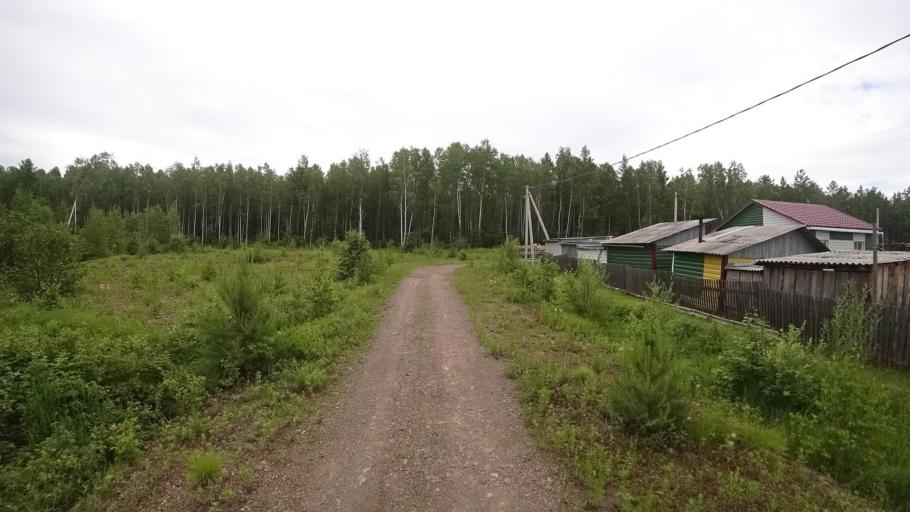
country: RU
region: Khabarovsk Krai
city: Amursk
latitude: 49.8942
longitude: 136.1639
